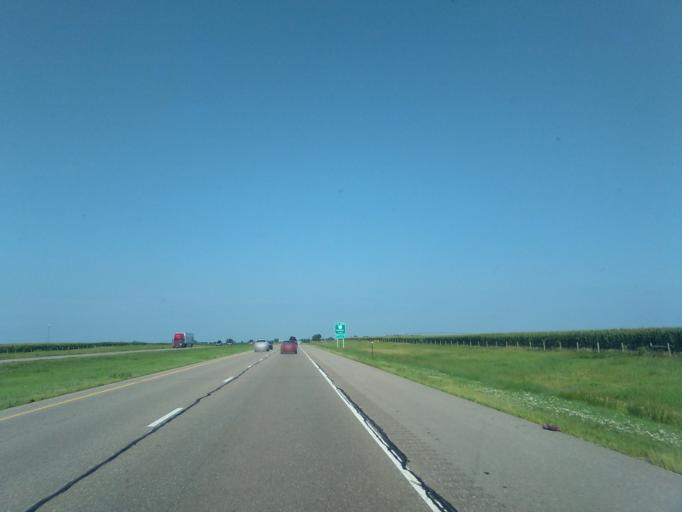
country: US
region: Nebraska
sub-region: Hamilton County
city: Aurora
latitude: 40.8221
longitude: -98.1763
